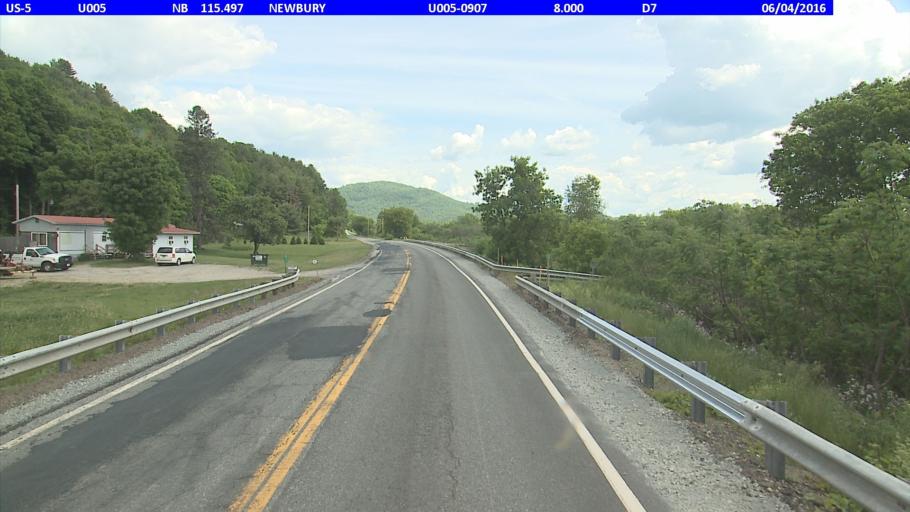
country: US
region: New Hampshire
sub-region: Grafton County
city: Woodsville
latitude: 44.1332
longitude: -72.0436
